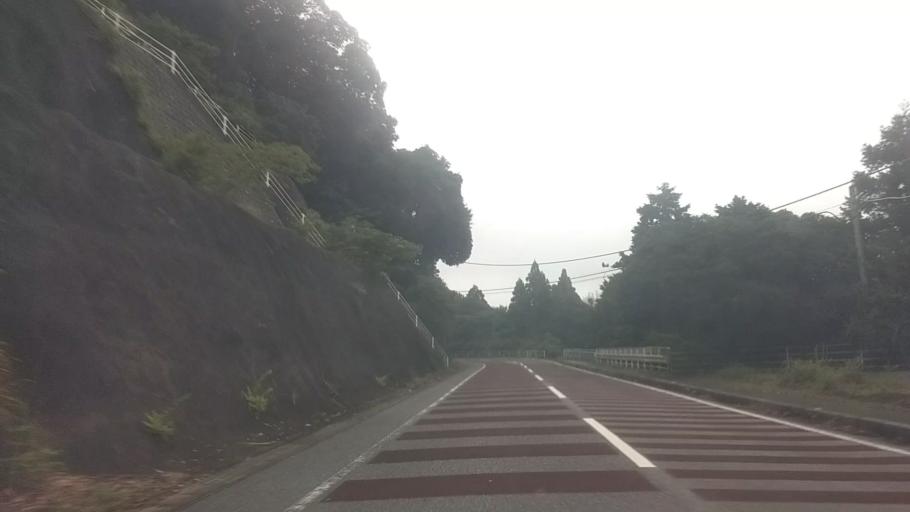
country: JP
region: Chiba
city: Kawaguchi
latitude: 35.1496
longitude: 140.1490
